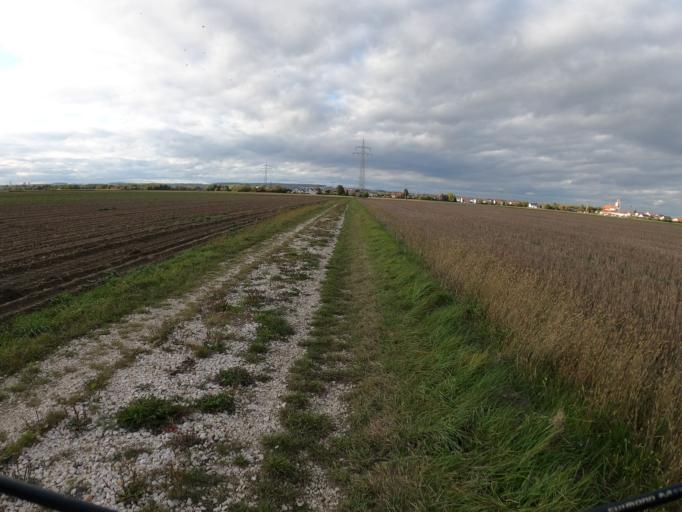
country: DE
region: Bavaria
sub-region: Swabia
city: Nersingen
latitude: 48.4183
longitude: 10.1249
